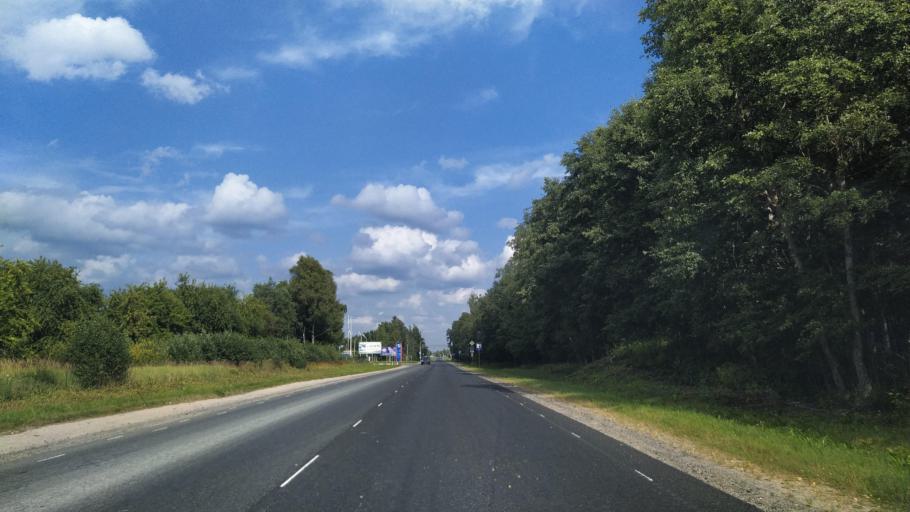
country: RU
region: Pskov
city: Porkhov
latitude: 57.7553
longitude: 29.5235
